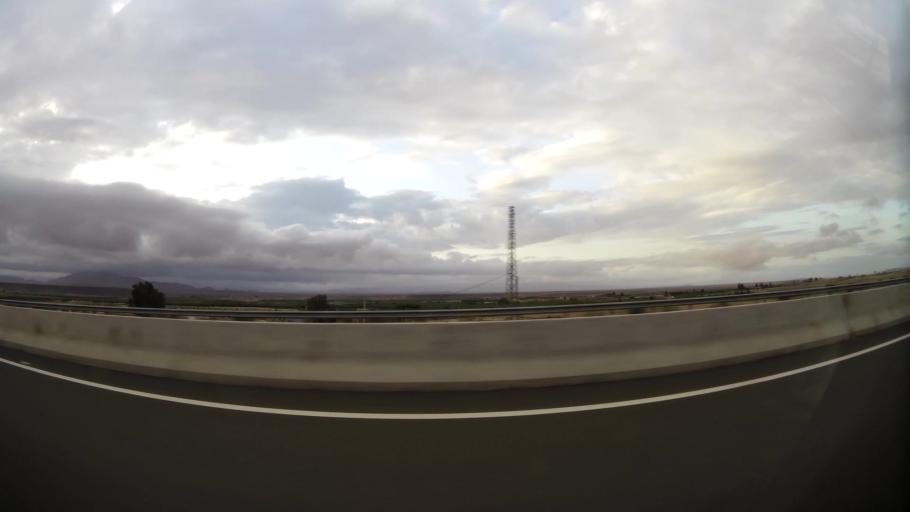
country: MA
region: Taza-Al Hoceima-Taounate
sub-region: Taza
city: Guercif
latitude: 34.4025
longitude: -3.1880
